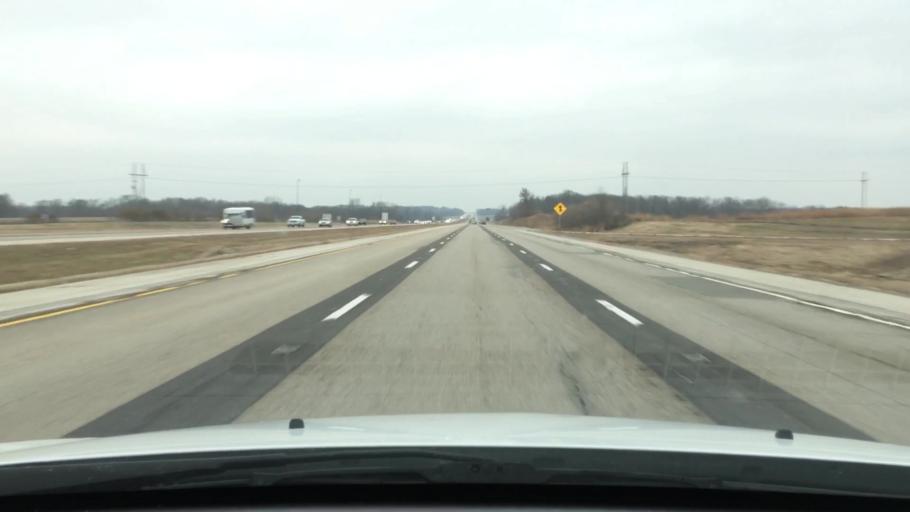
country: US
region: Illinois
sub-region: Logan County
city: Lincoln
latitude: 40.1147
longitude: -89.4164
